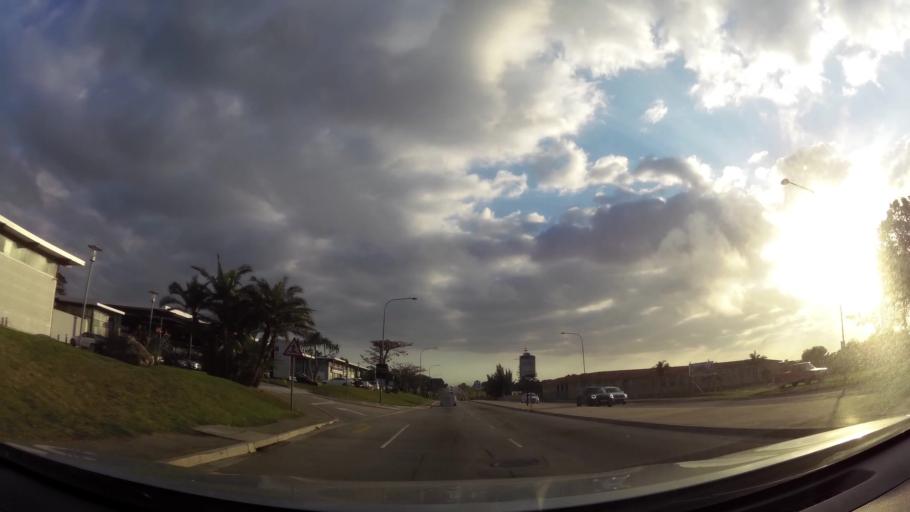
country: ZA
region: Eastern Cape
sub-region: Nelson Mandela Bay Metropolitan Municipality
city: Port Elizabeth
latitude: -33.9783
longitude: 25.5537
